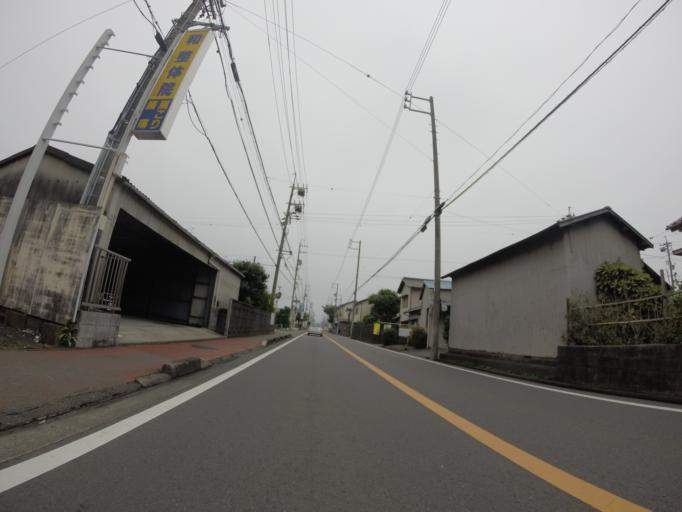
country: JP
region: Shizuoka
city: Shizuoka-shi
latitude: 34.9477
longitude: 138.3989
